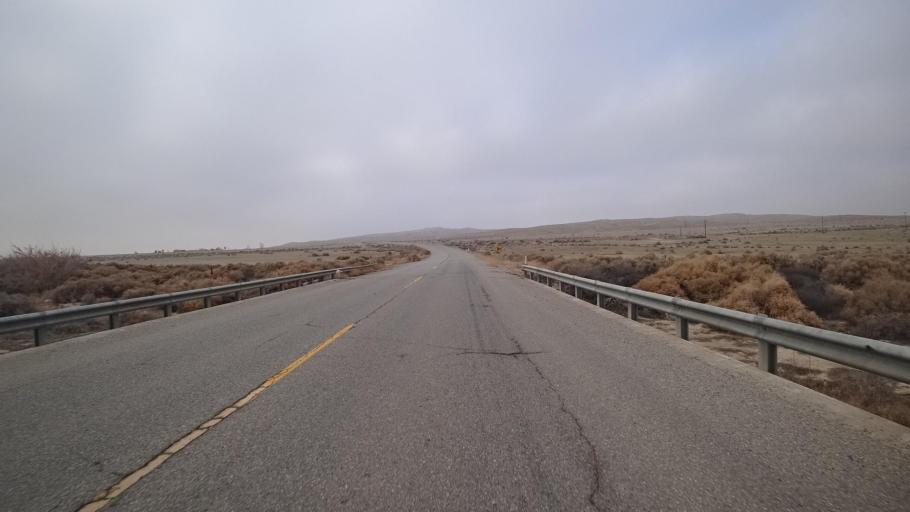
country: US
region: California
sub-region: Kern County
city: Maricopa
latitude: 35.1272
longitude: -119.3650
